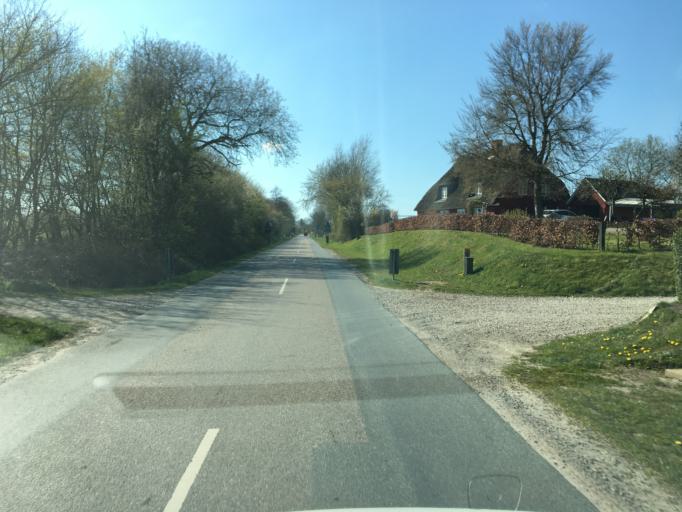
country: DK
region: South Denmark
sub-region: Sonderborg Kommune
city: Grasten
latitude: 54.9046
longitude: 9.5652
